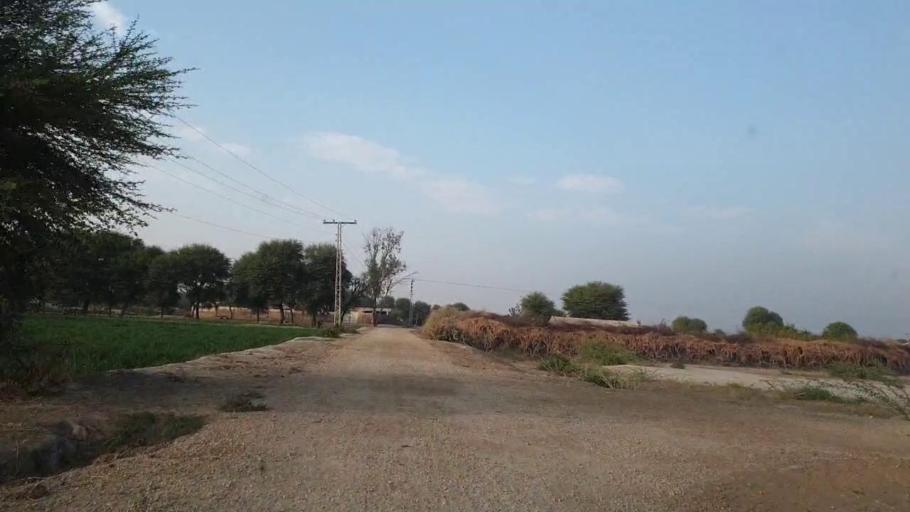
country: PK
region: Sindh
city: Pithoro
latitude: 25.5837
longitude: 69.3540
